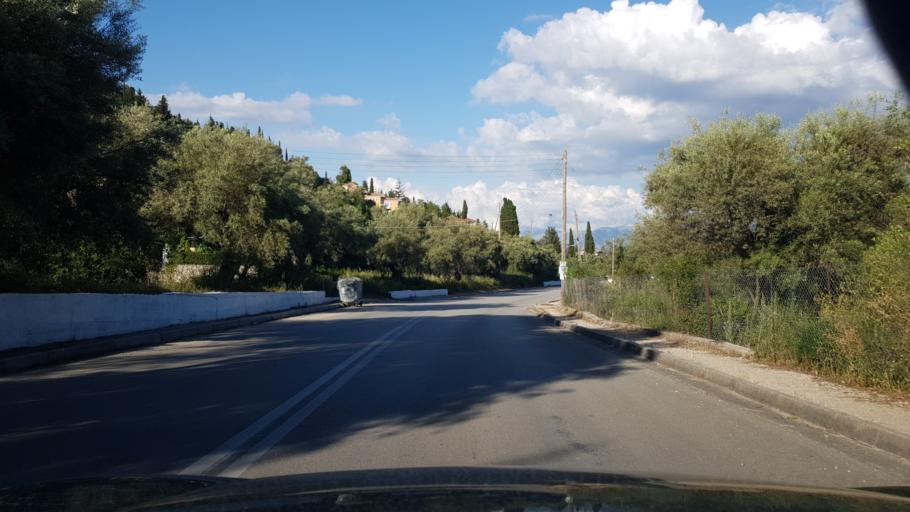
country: GR
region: Ionian Islands
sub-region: Lefkada
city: Nidri
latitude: 38.7161
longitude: 20.7130
